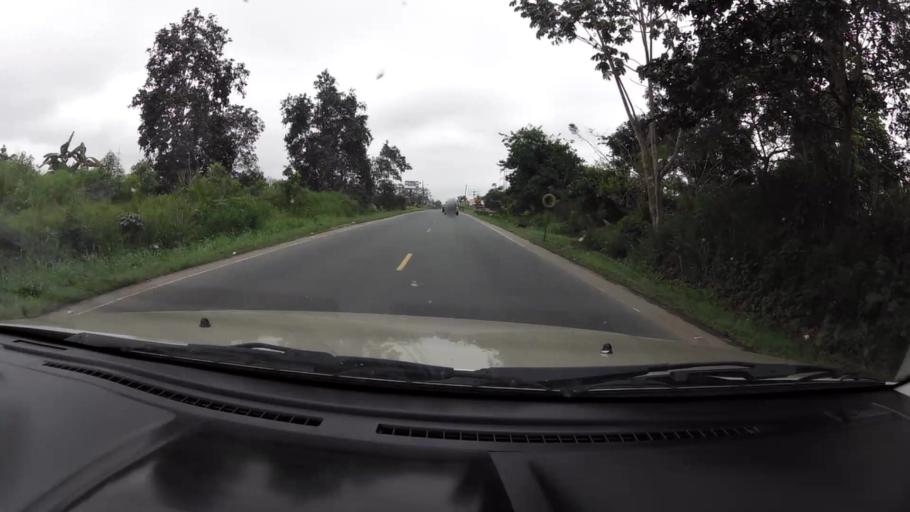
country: EC
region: El Oro
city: Pasaje
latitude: -3.1303
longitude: -79.7771
